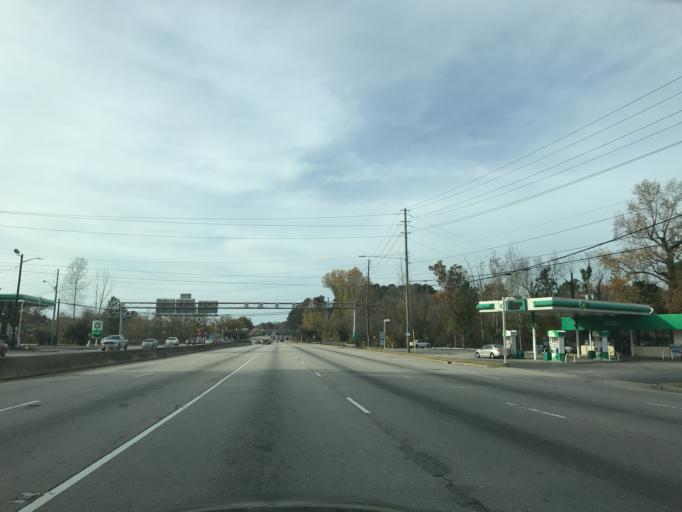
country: US
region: North Carolina
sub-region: Wake County
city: West Raleigh
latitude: 35.8371
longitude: -78.6721
